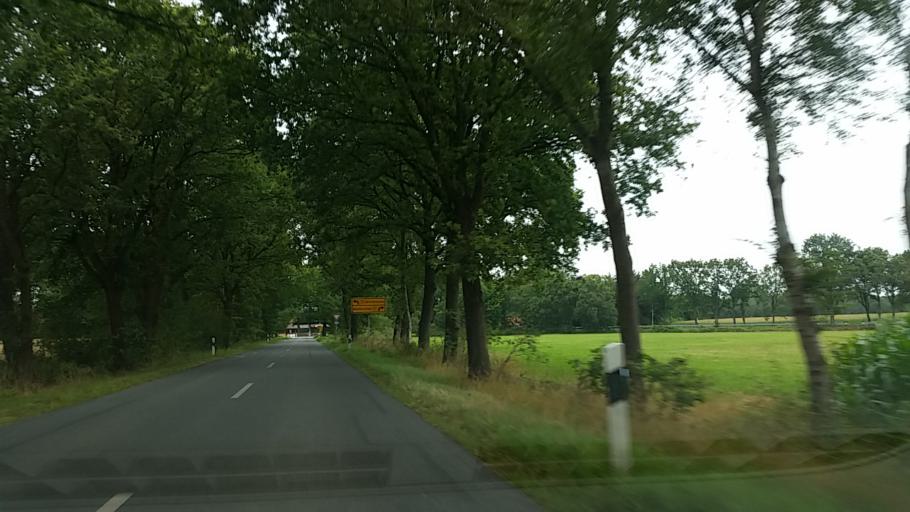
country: DE
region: Lower Saxony
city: Beverstedt
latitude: 53.4237
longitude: 8.9036
